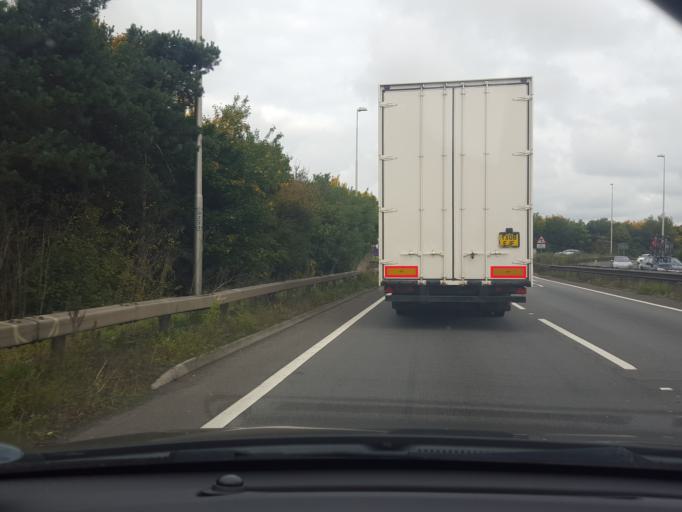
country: GB
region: England
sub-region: Suffolk
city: Bramford
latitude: 52.0345
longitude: 1.0969
